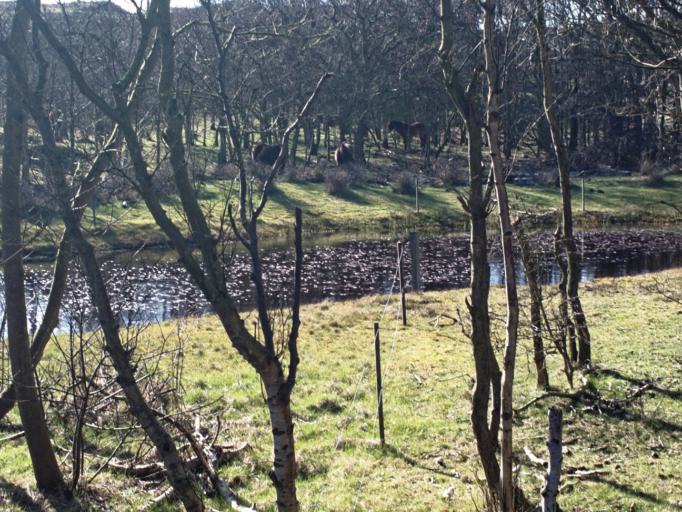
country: NL
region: North Holland
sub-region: Gemeente Texel
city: Den Burg
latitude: 53.0406
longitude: 4.7360
